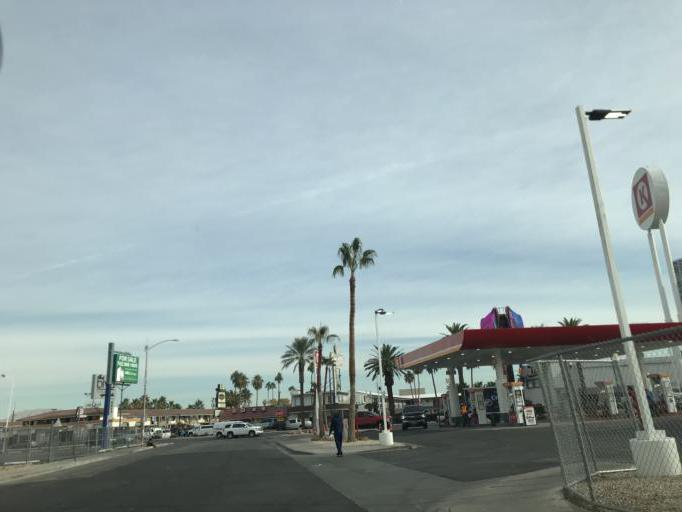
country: US
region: Nevada
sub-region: Clark County
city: Las Vegas
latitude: 36.1454
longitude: -115.1574
